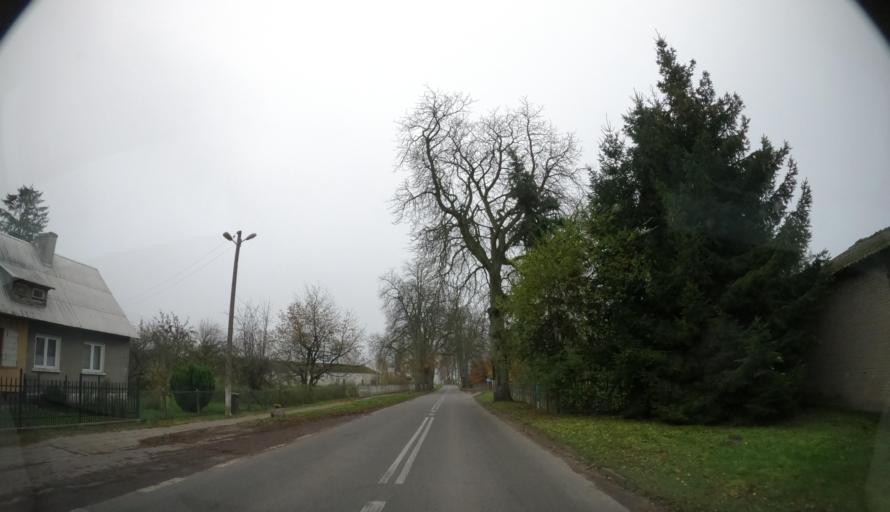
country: PL
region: West Pomeranian Voivodeship
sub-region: Powiat lobeski
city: Radowo Male
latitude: 53.6850
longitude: 15.4215
